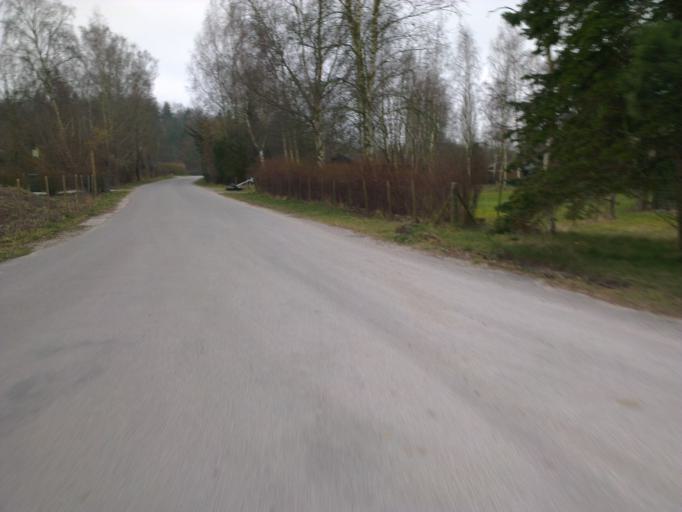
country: DK
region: Capital Region
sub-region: Frederikssund Kommune
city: Frederikssund
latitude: 55.7918
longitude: 12.0489
